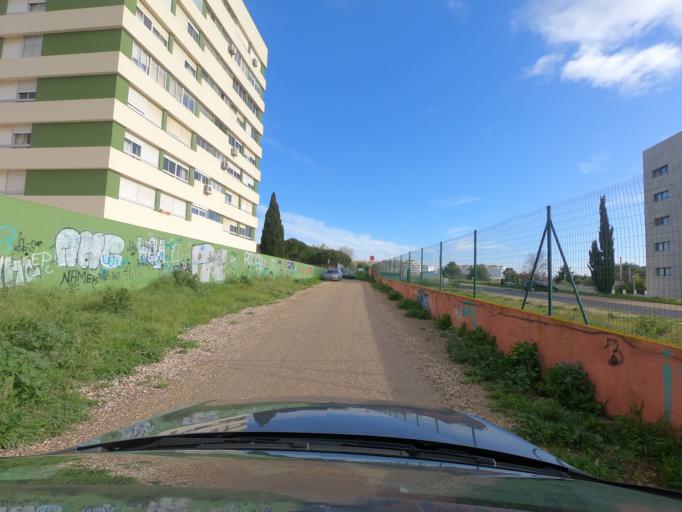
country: PT
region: Lisbon
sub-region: Oeiras
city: Carcavelos
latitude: 38.6956
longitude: -9.3227
